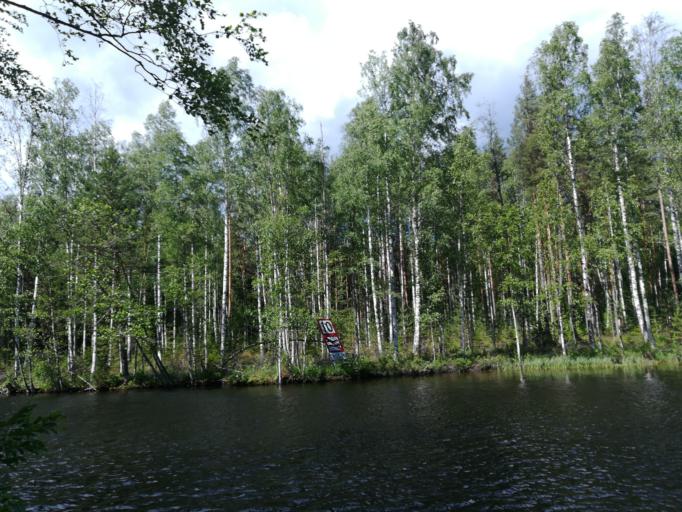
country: FI
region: Southern Savonia
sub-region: Mikkeli
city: Hirvensalmi
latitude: 61.6281
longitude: 26.7623
